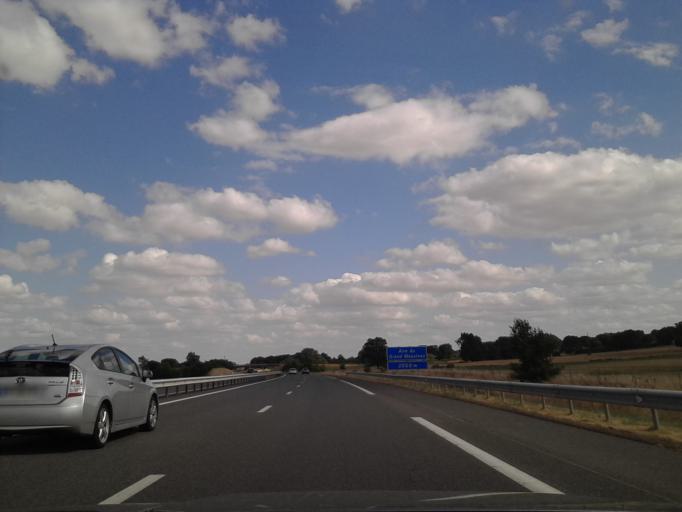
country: FR
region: Auvergne
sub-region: Departement de l'Allier
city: Vallon-en-Sully
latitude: 46.5302
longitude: 2.5620
